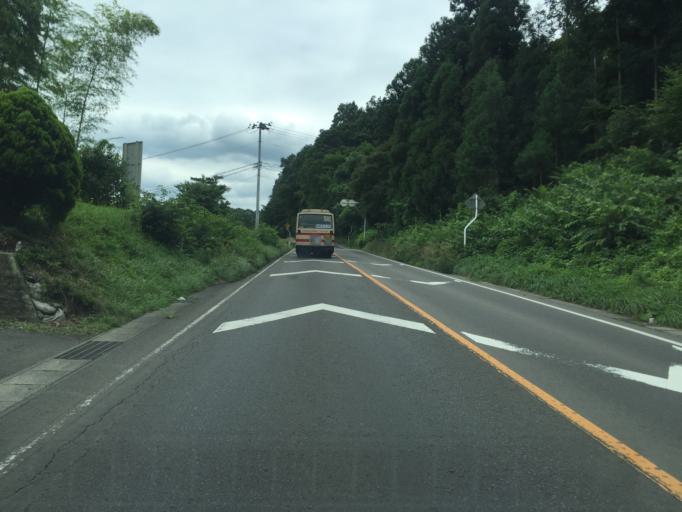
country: JP
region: Fukushima
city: Fukushima-shi
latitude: 37.7156
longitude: 140.4628
